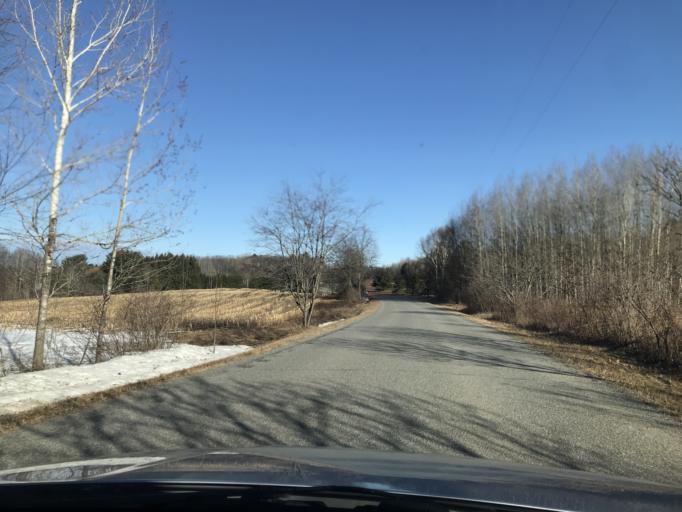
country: US
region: Wisconsin
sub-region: Marinette County
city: Niagara
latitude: 45.3838
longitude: -88.0408
